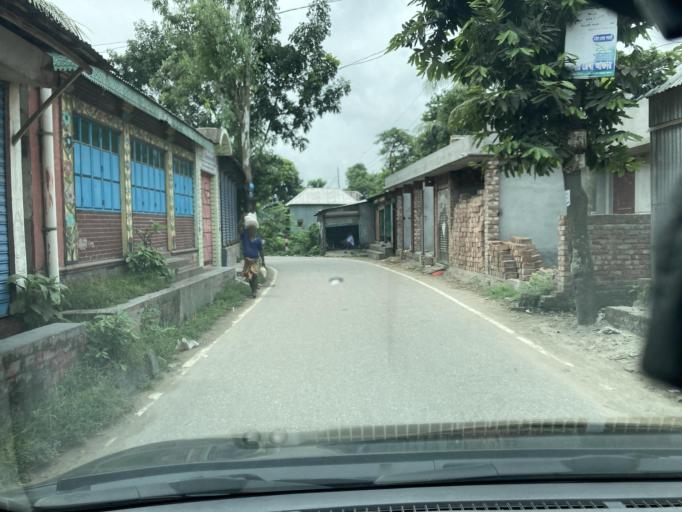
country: BD
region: Dhaka
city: Dohar
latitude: 23.7607
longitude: 90.2050
